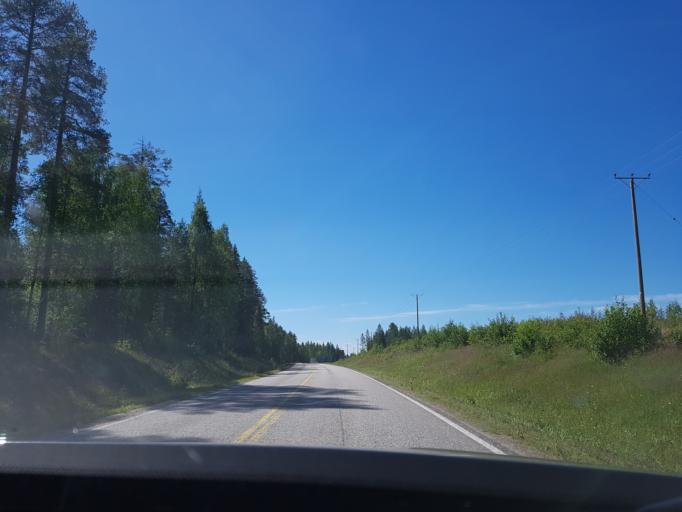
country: FI
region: Kainuu
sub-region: Kehys-Kainuu
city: Kuhmo
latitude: 64.1741
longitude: 29.6599
